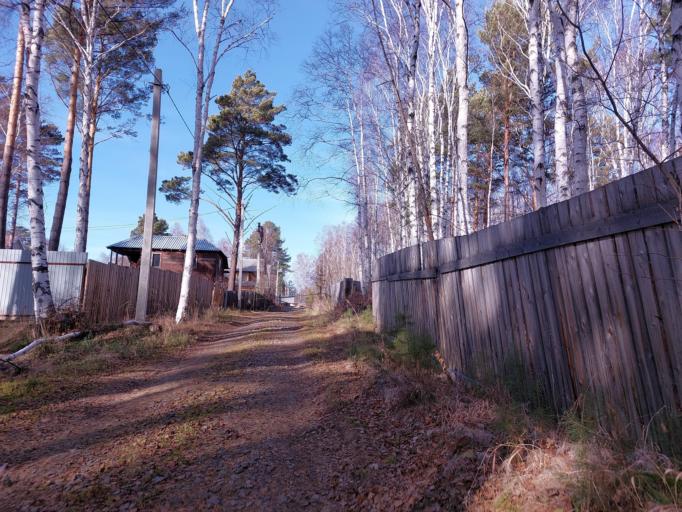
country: RU
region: Irkutsk
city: Pivovarikha
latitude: 52.1855
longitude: 104.4560
